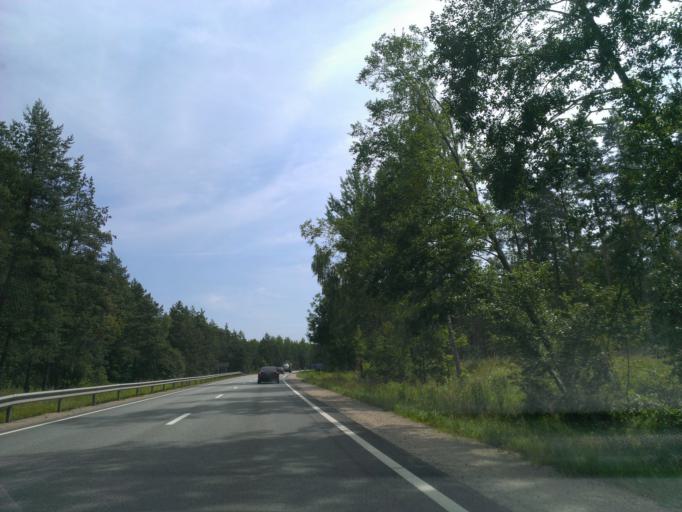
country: LV
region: Riga
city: Bergi
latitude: 56.9658
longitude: 24.3645
